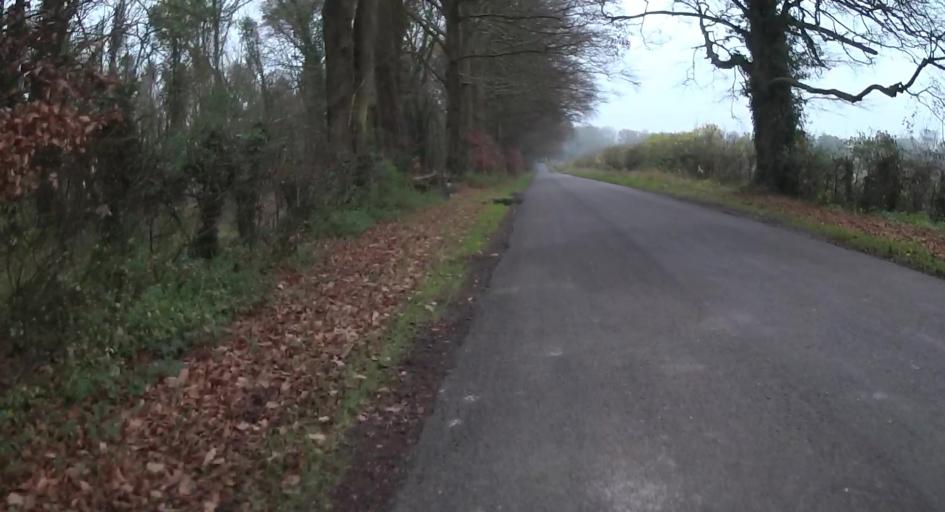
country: GB
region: England
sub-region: Hampshire
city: Kings Worthy
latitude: 51.1218
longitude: -1.2112
